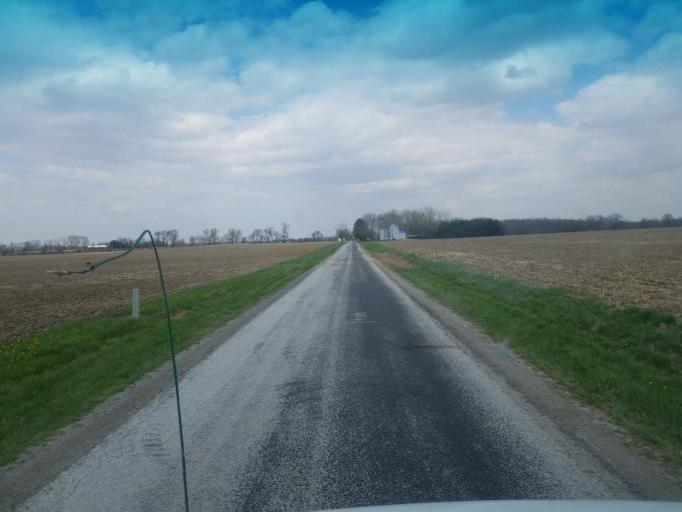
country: US
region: Ohio
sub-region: Wyandot County
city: Upper Sandusky
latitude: 40.9381
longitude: -83.2365
